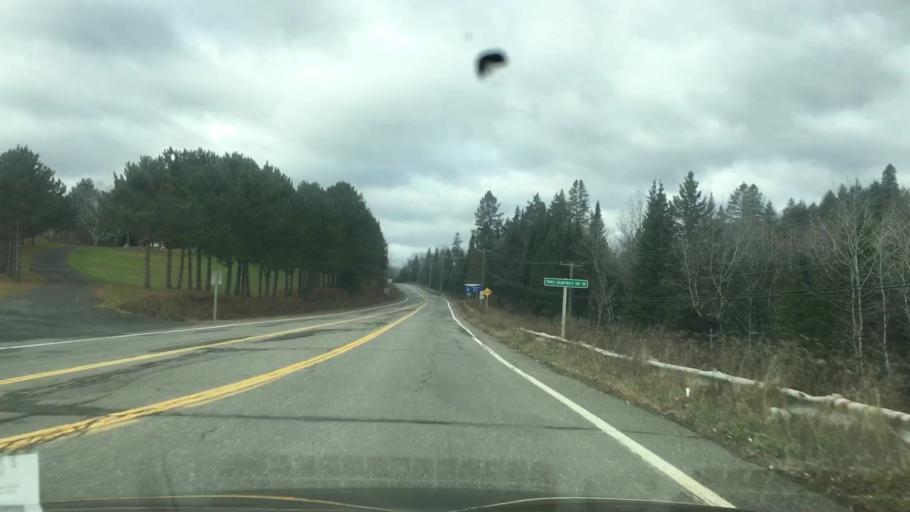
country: US
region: Maine
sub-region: Aroostook County
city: Fort Fairfield
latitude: 46.7499
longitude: -67.7205
